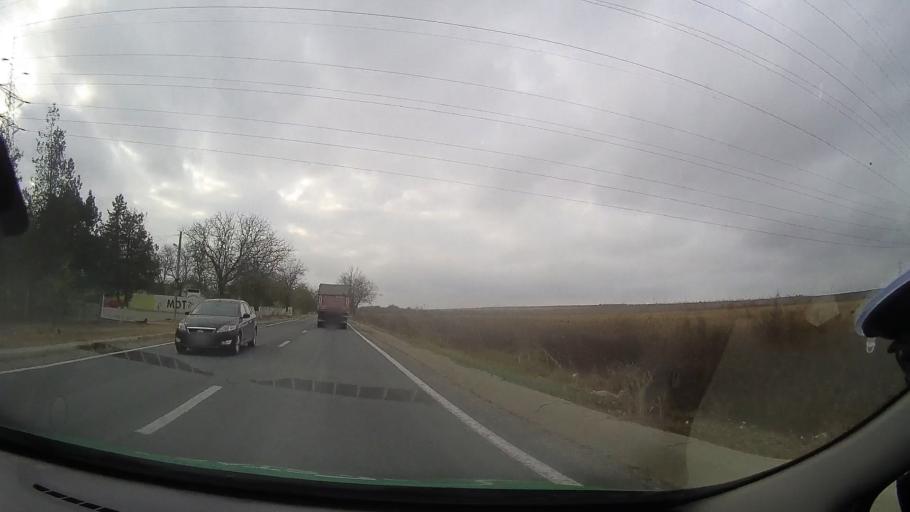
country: RO
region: Constanta
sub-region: Municipiul Medgidia
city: Medgidia
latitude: 44.2678
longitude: 28.2688
